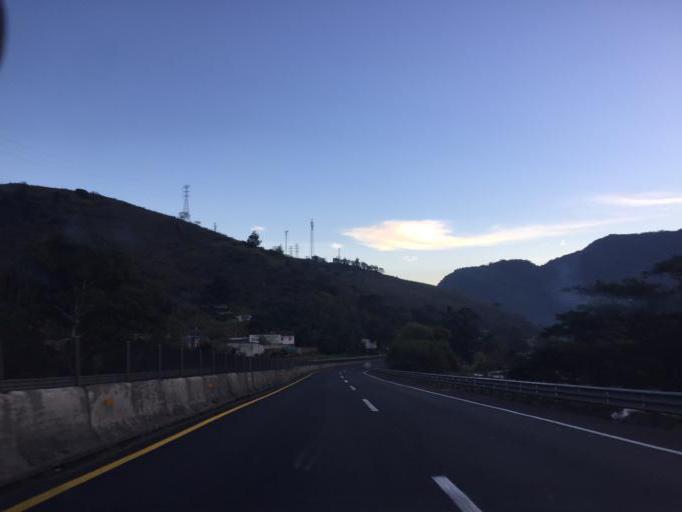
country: MX
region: Veracruz
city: Ciudad Mendoza
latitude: 18.8167
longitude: -97.1745
